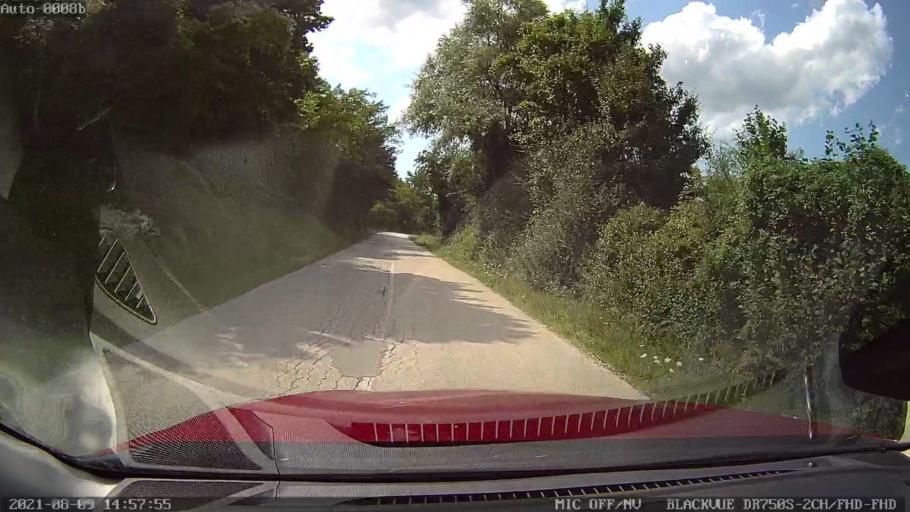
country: HR
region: Istarska
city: Pazin
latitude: 45.2646
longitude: 14.0462
